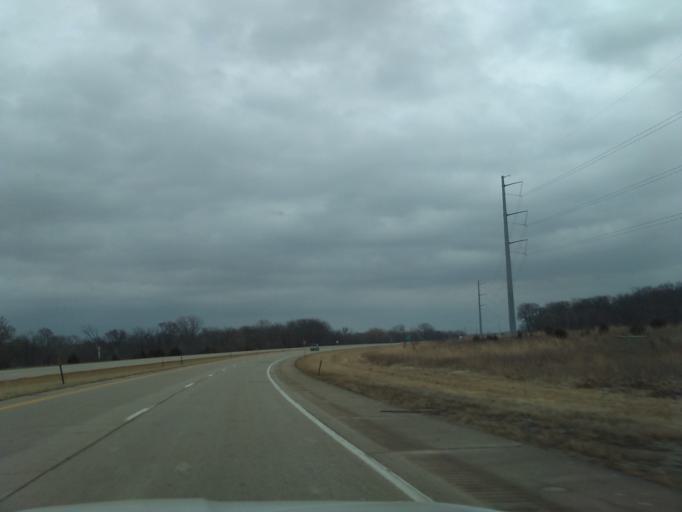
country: US
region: Nebraska
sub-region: Otoe County
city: Syracuse
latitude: 40.6767
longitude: -96.0386
